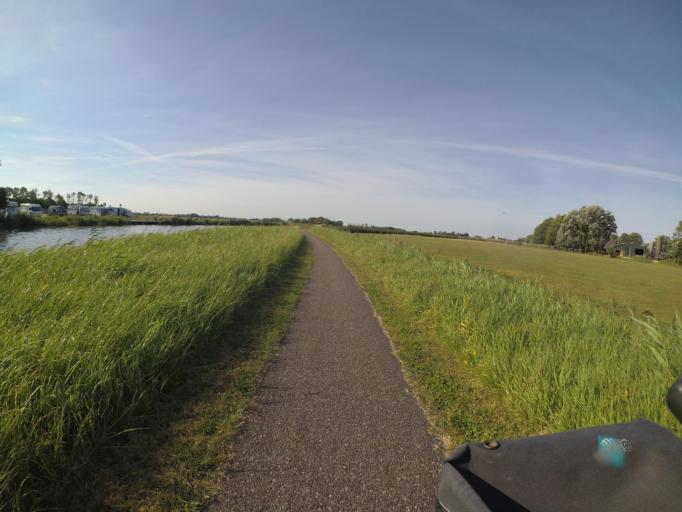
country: NL
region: Friesland
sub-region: Gemeente Dantumadiel
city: Rinsumageast
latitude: 53.3186
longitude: 5.9497
